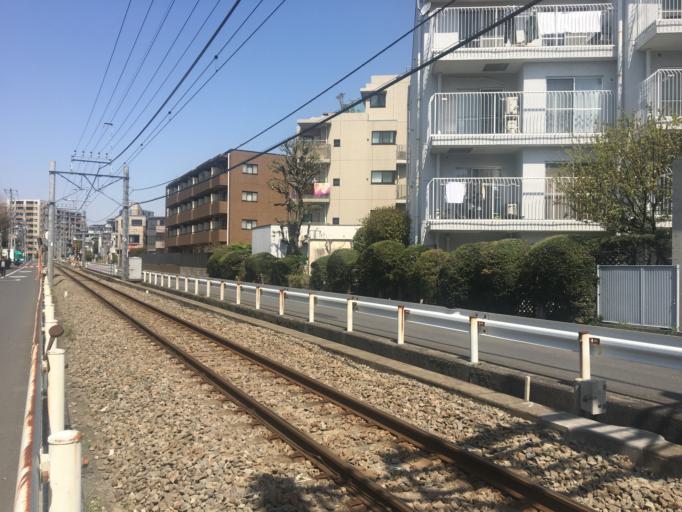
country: JP
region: Tokyo
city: Kokubunji
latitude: 35.7023
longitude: 139.4794
